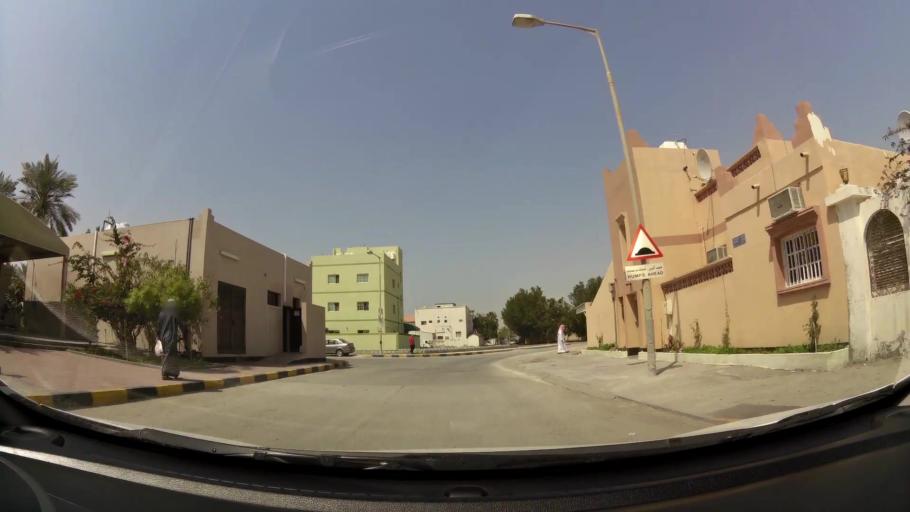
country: BH
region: Manama
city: Jidd Hafs
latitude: 26.2130
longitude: 50.4487
